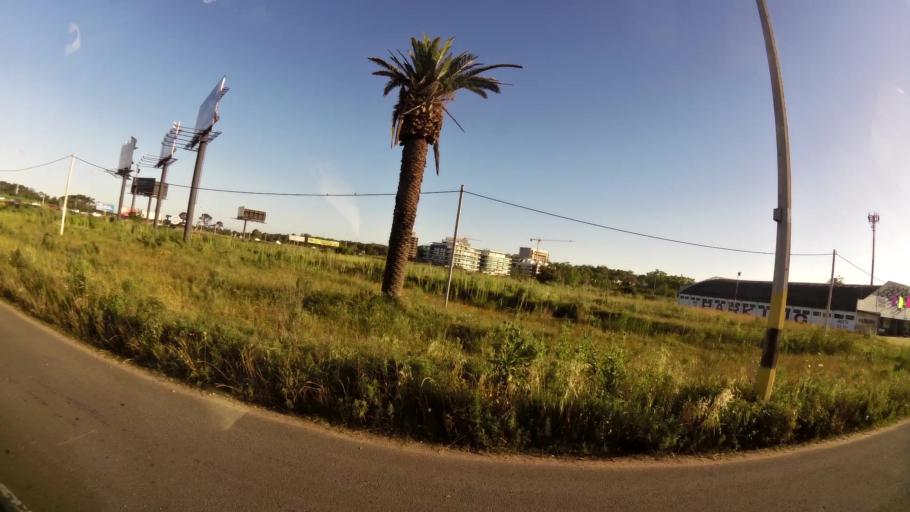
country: UY
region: Canelones
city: Paso de Carrasco
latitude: -34.8462
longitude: -56.0256
